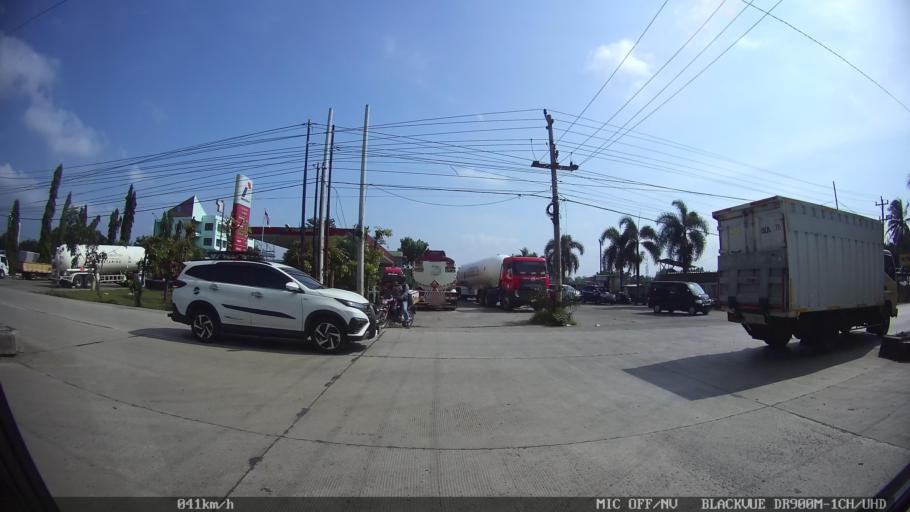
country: ID
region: Lampung
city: Kedaton
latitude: -5.3596
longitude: 105.2342
